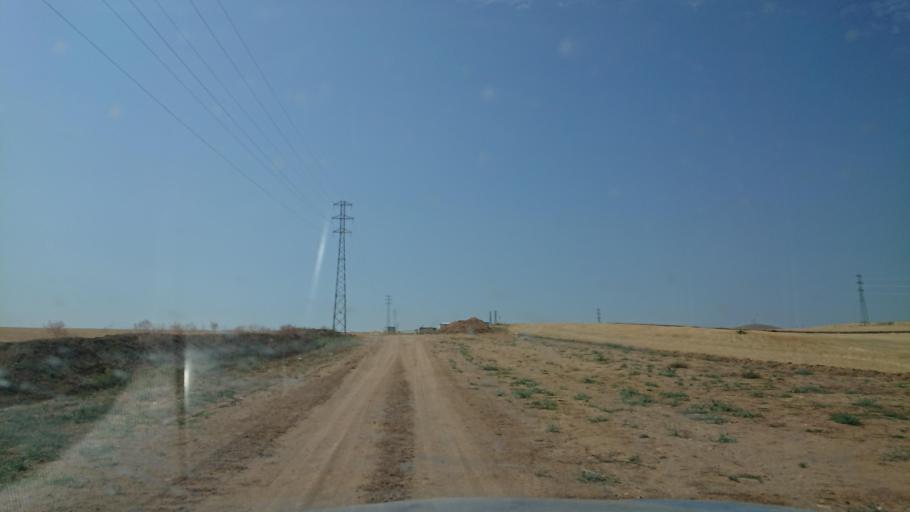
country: TR
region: Aksaray
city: Sariyahsi
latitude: 38.9532
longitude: 33.9132
